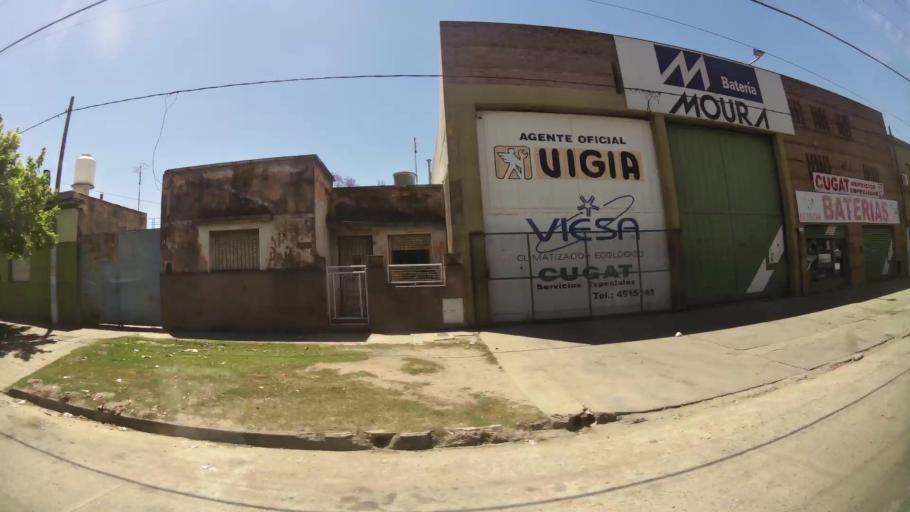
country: AR
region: Cordoba
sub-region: Departamento de Capital
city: Cordoba
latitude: -31.3933
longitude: -64.1522
